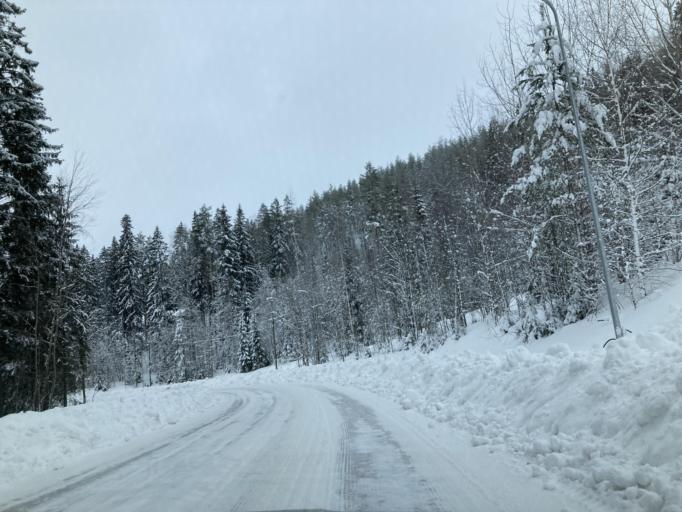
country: FI
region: Central Finland
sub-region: Jaemsae
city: Jaemsae
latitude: 61.8769
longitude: 25.3118
